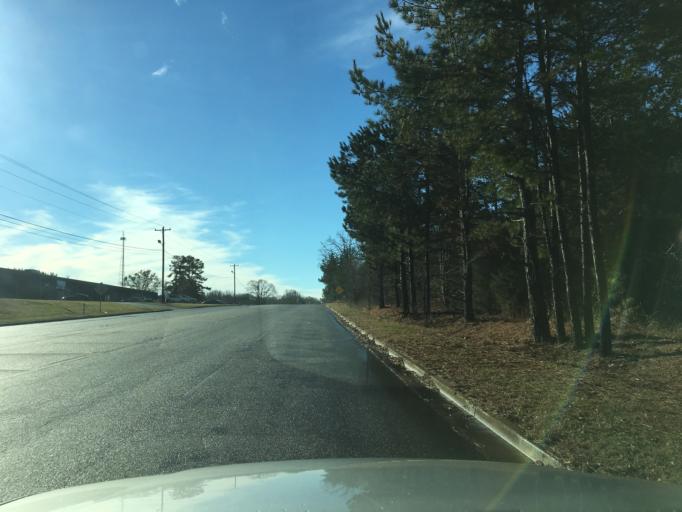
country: US
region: South Carolina
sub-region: Spartanburg County
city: Mayo
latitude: 35.0183
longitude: -81.8729
